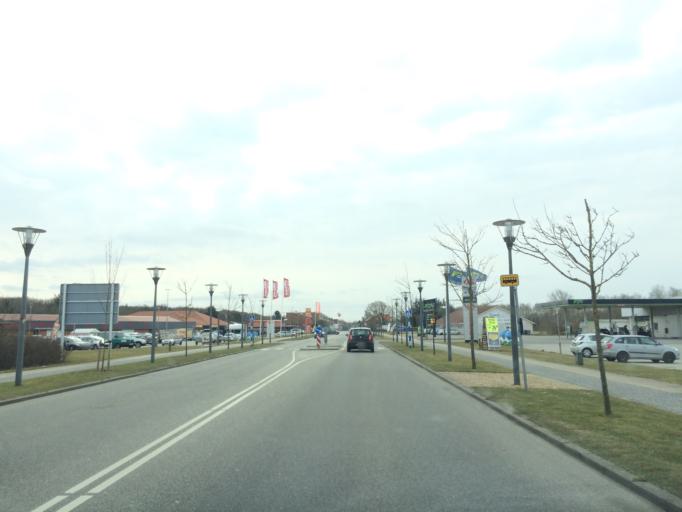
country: DK
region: Central Jutland
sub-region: Ringkobing-Skjern Kommune
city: Tarm
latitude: 55.9167
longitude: 8.5181
